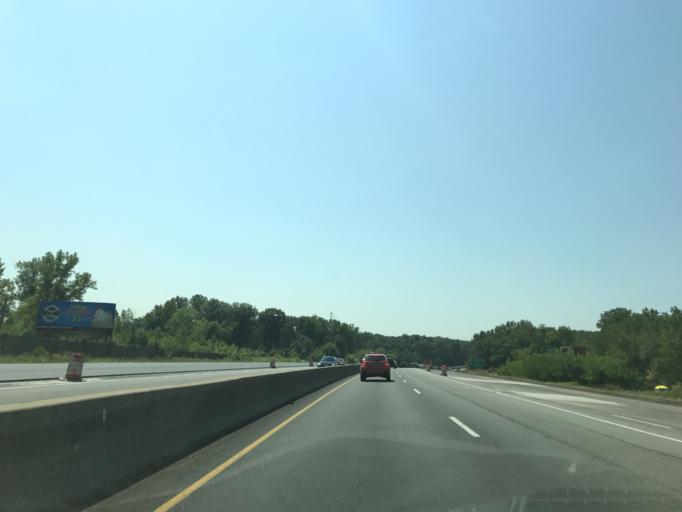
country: US
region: Indiana
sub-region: Porter County
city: Burns Harbor
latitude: 41.6034
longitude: -87.1415
